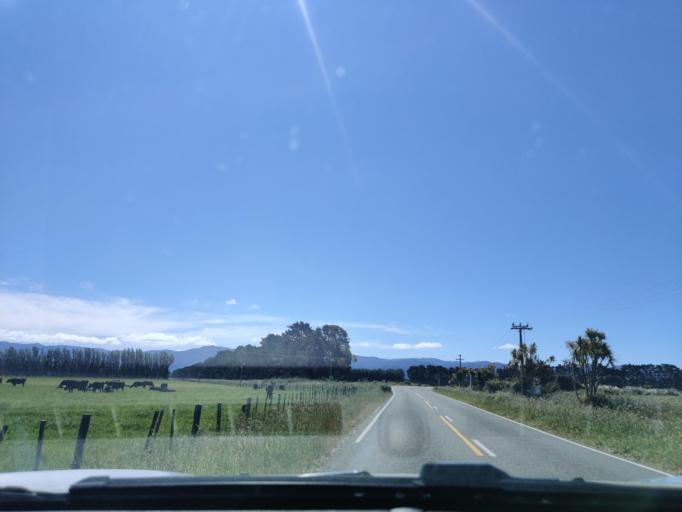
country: NZ
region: Wellington
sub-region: Upper Hutt City
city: Upper Hutt
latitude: -41.2826
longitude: 175.2664
